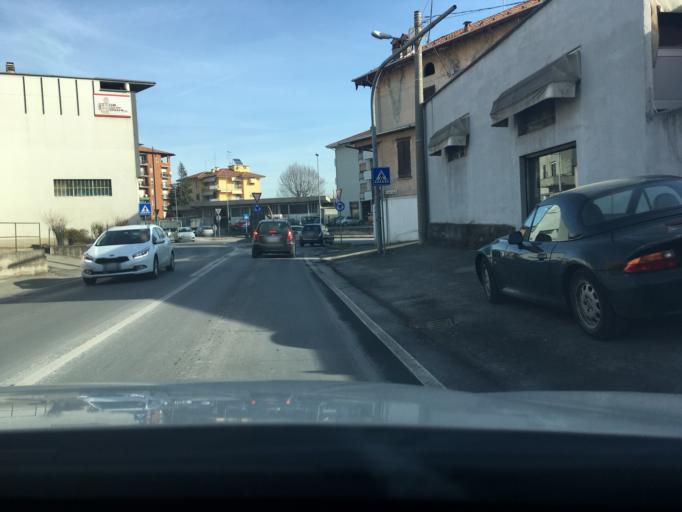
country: IT
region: Piedmont
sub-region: Provincia di Novara
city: Borgomanero
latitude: 45.6929
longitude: 8.4687
